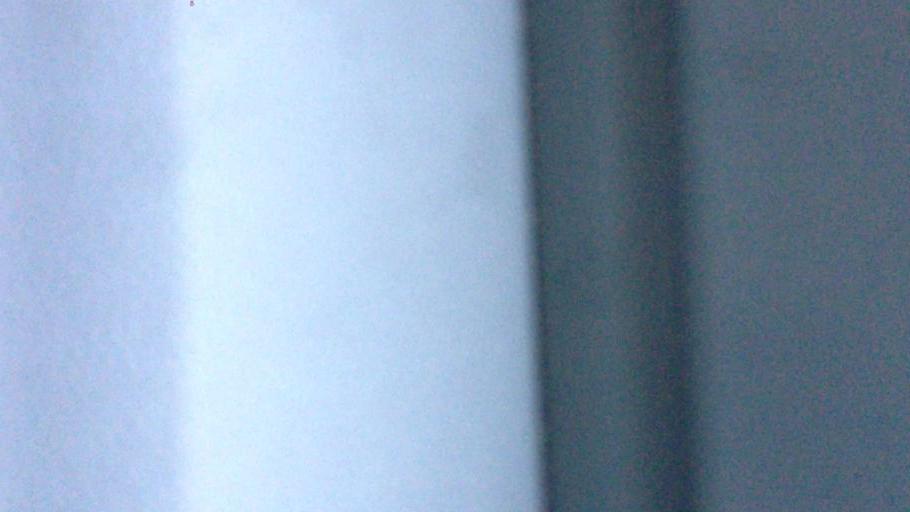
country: US
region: New York
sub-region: Dutchess County
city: Rhinebeck
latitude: 41.9570
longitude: -73.9198
